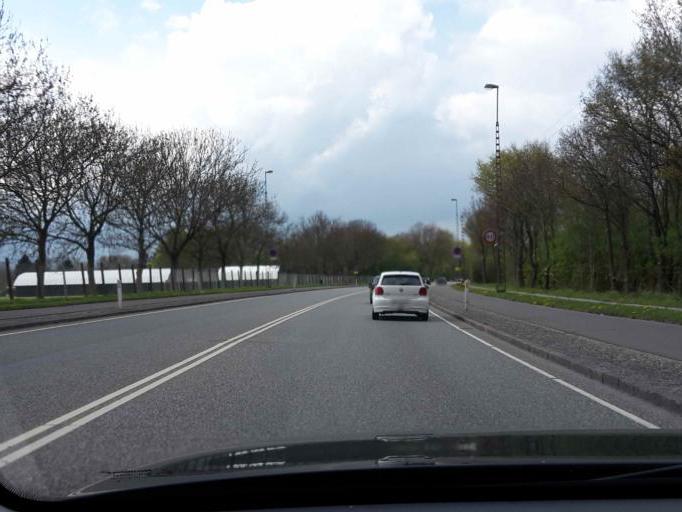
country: DK
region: South Denmark
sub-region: Odense Kommune
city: Odense
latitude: 55.3827
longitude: 10.3607
